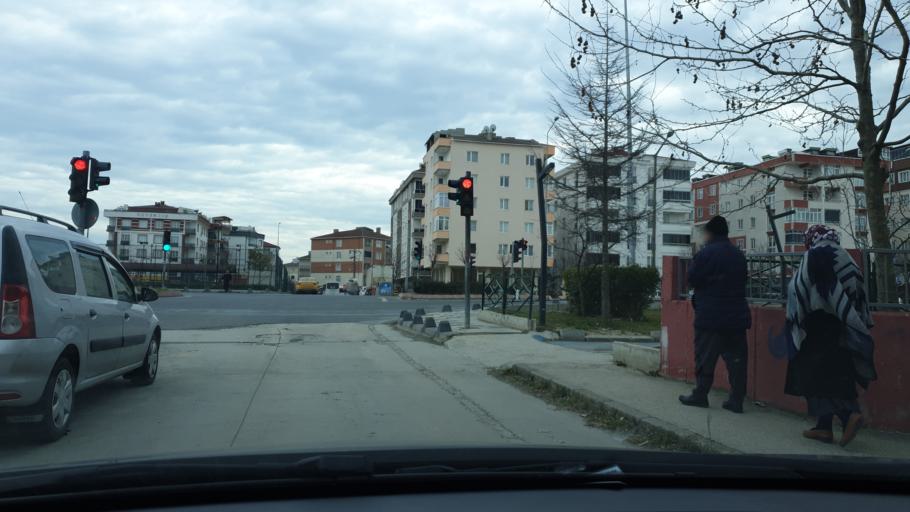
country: TR
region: Tekirdag
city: Cerkezkoey
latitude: 41.2819
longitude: 27.9826
